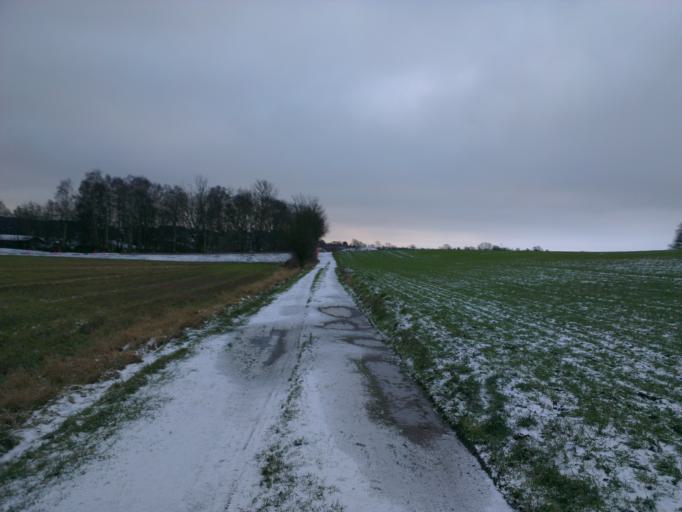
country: DK
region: Capital Region
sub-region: Frederikssund Kommune
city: Jaegerspris
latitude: 55.8615
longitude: 11.9938
